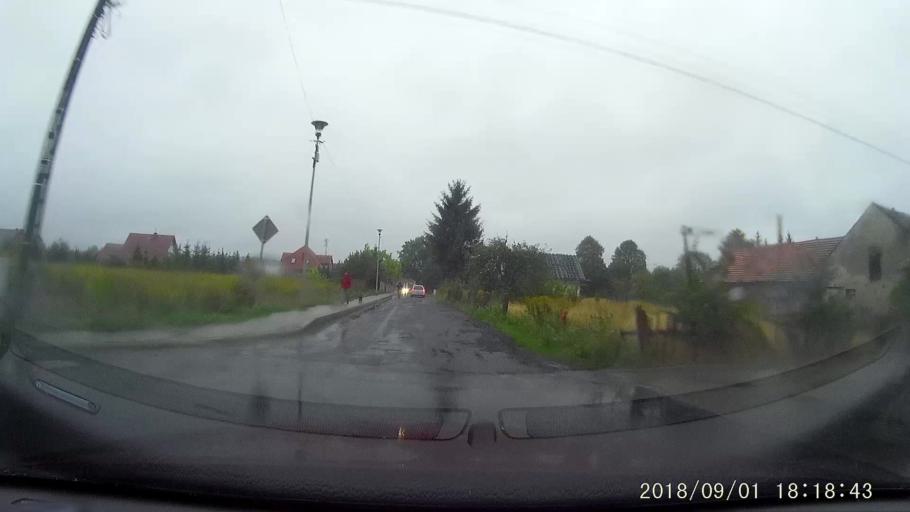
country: PL
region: Lower Silesian Voivodeship
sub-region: Powiat zgorzelecki
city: Piensk
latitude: 51.2583
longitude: 15.0457
